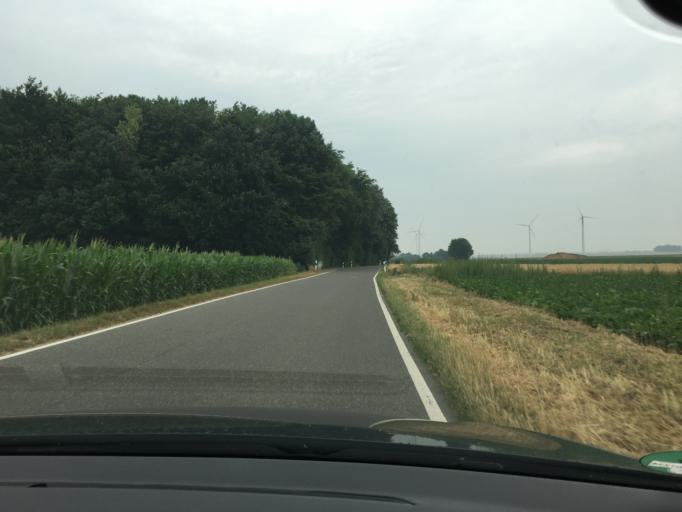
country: DE
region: North Rhine-Westphalia
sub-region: Regierungsbezirk Koln
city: Titz
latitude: 51.0548
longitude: 6.4047
